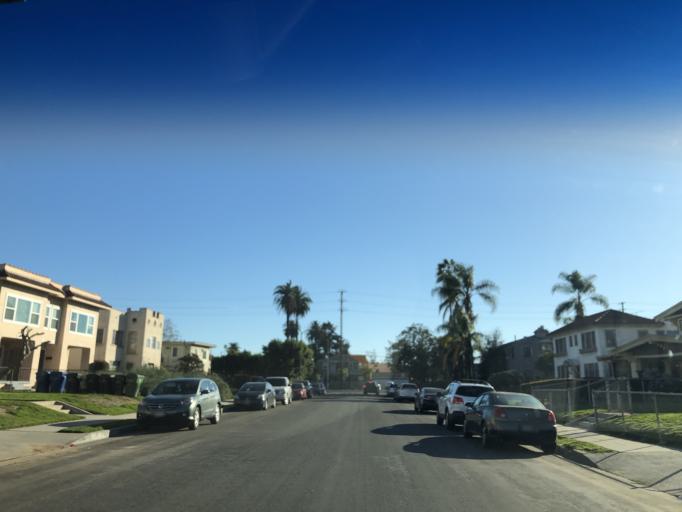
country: US
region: California
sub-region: Los Angeles County
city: Hollywood
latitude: 34.0445
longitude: -118.3157
